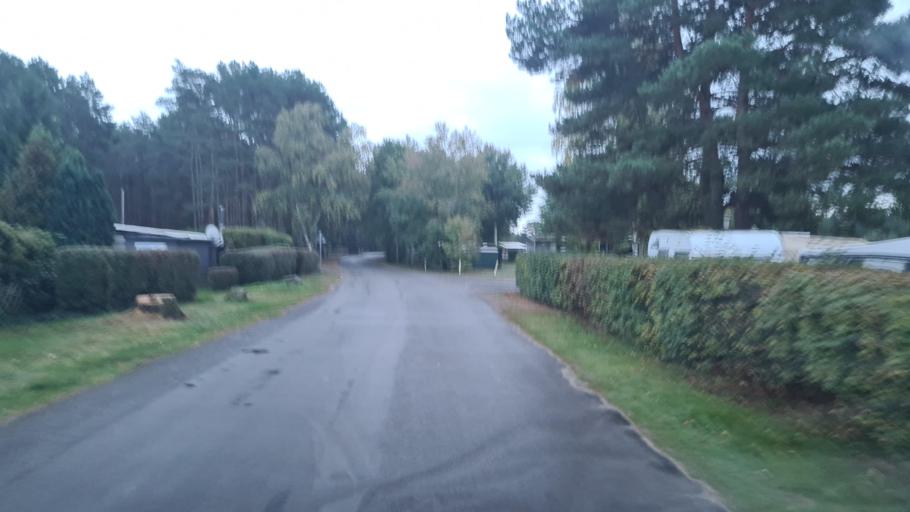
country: DE
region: Brandenburg
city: Munchehofe
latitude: 52.1276
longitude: 13.9441
